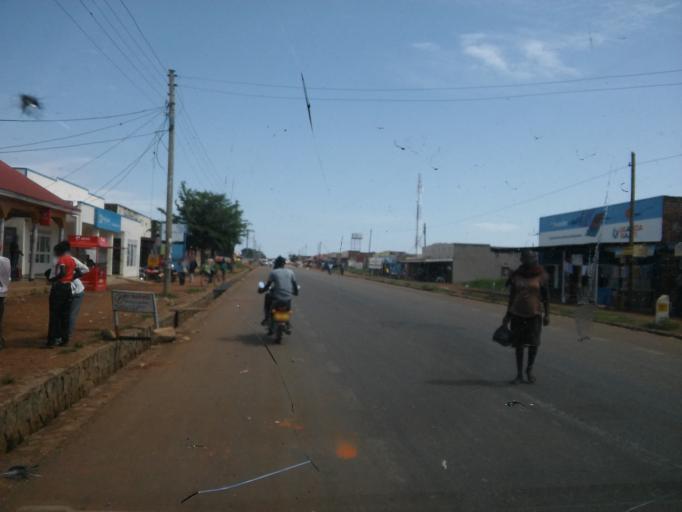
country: UG
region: Eastern Region
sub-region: Bukedea District
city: Bukedea
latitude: 1.3472
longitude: 34.0450
